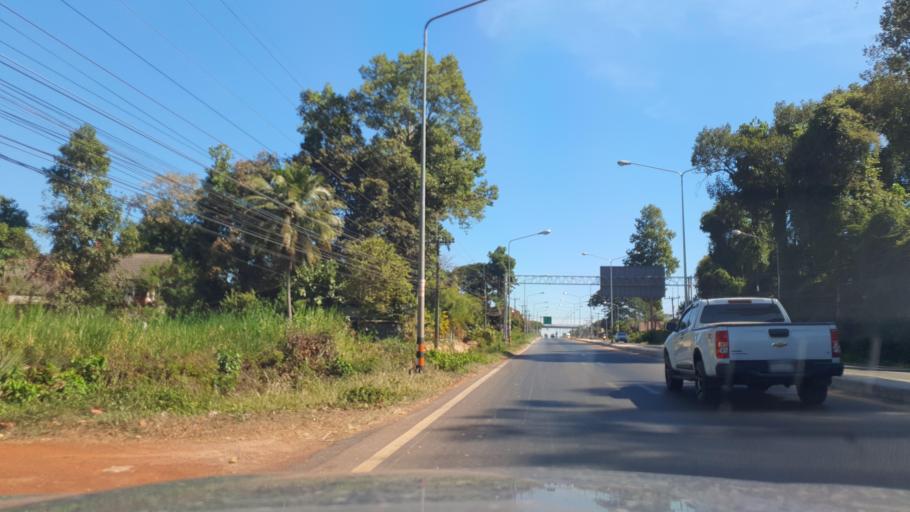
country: TH
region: Sakon Nakhon
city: Sakon Nakhon
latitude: 17.0851
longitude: 104.1871
